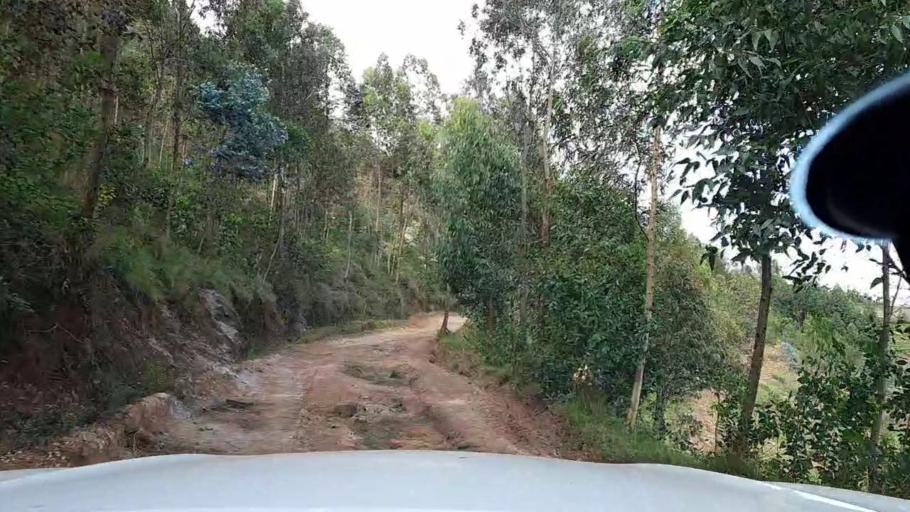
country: RW
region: Kigali
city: Kigali
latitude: -1.7855
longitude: 29.8324
